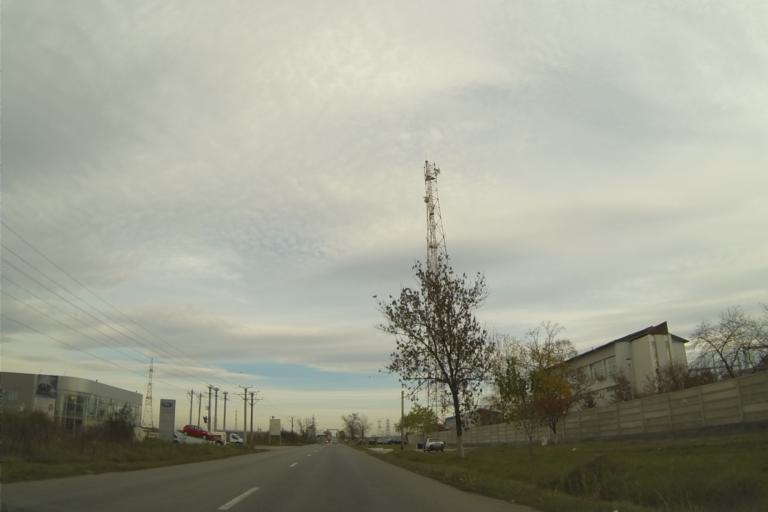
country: RO
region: Olt
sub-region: Municipiul Slatina
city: Slatina
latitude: 44.4518
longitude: 24.3914
